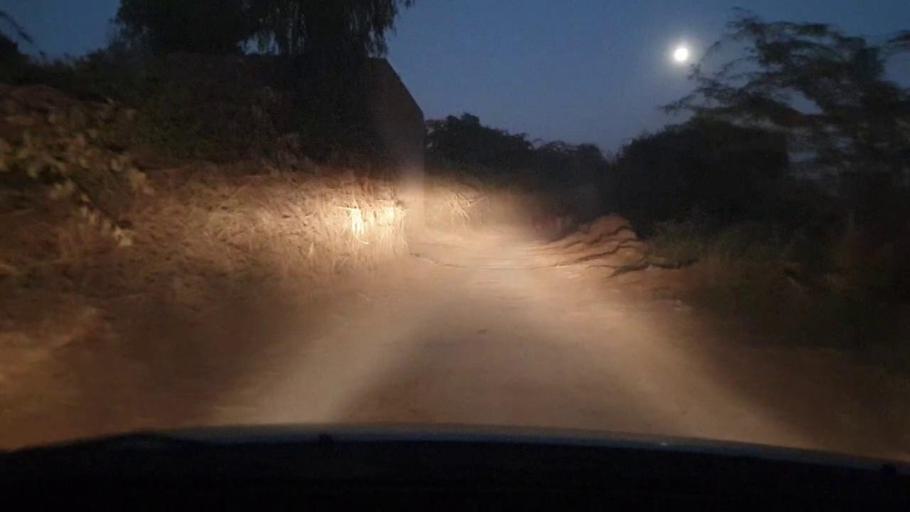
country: PK
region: Sindh
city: Khairpur Nathan Shah
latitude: 27.1354
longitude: 67.7355
